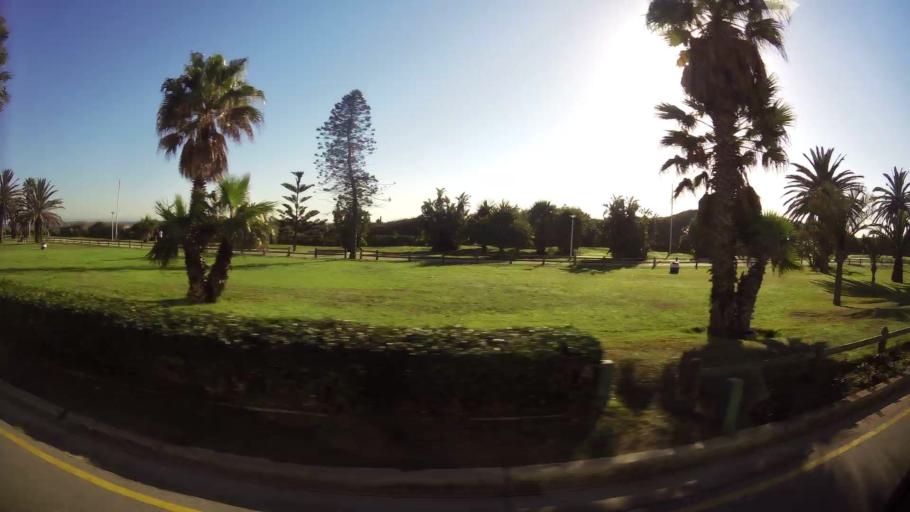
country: ZA
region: Eastern Cape
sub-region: Nelson Mandela Bay Metropolitan Municipality
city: Port Elizabeth
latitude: -33.9829
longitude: 25.6640
